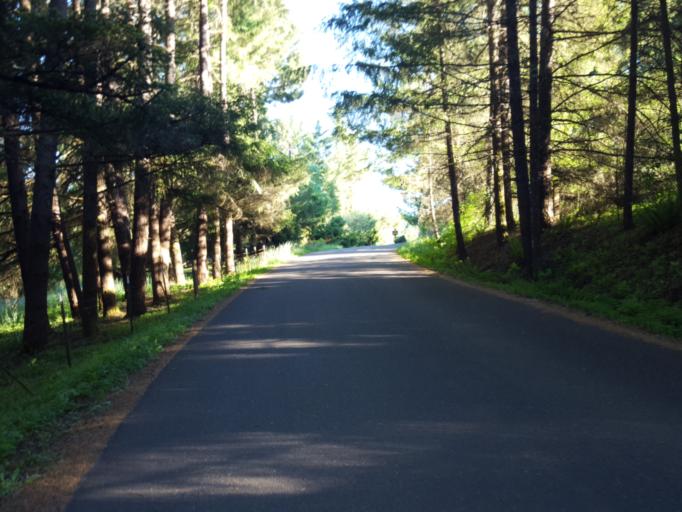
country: US
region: Oregon
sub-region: Yamhill County
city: McMinnville
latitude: 45.2251
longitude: -123.2688
